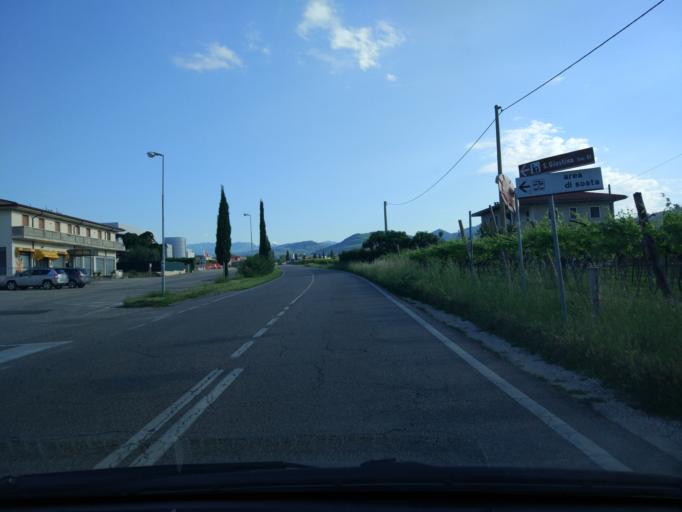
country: IT
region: Veneto
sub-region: Provincia di Verona
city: Illasi
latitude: 45.4561
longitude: 11.1772
